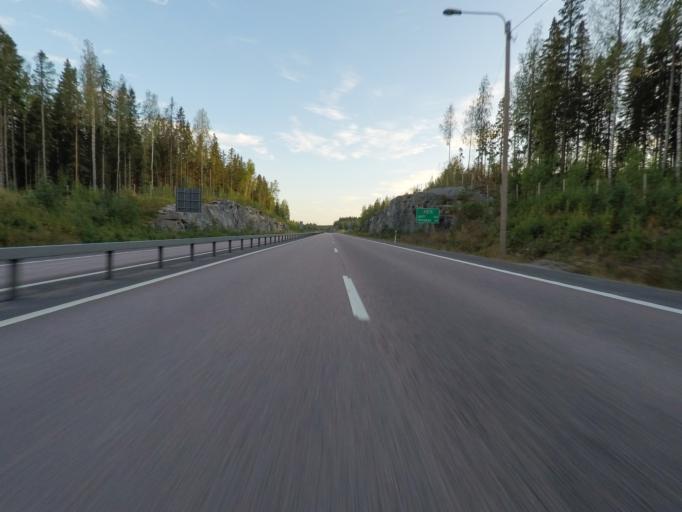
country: FI
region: Central Finland
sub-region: Jyvaeskylae
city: Saeynaetsalo
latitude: 62.2241
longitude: 25.8986
